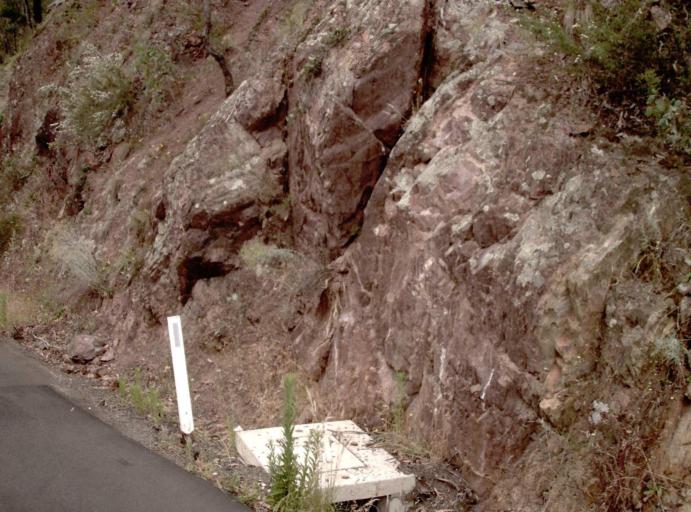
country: AU
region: Victoria
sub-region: Wellington
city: Heyfield
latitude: -37.7018
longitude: 146.6616
